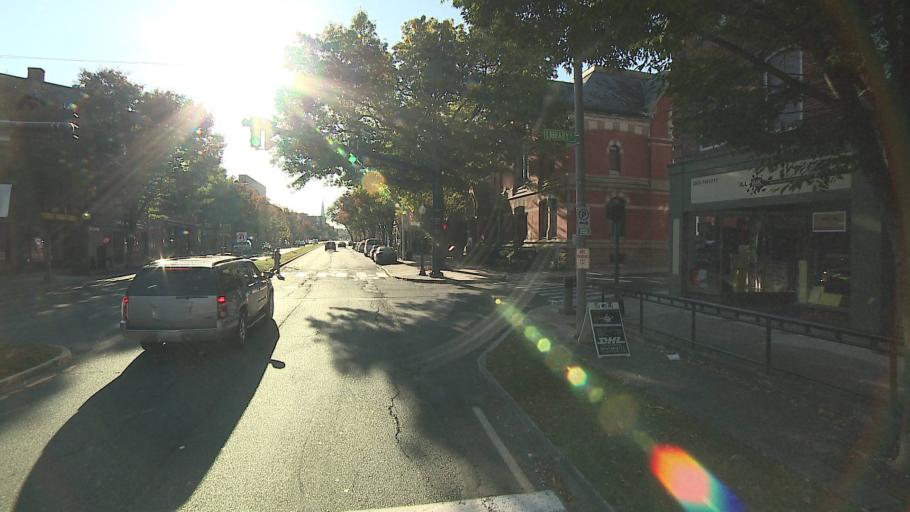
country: US
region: Connecticut
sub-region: Fairfield County
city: Danbury
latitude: 41.3955
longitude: -73.4536
